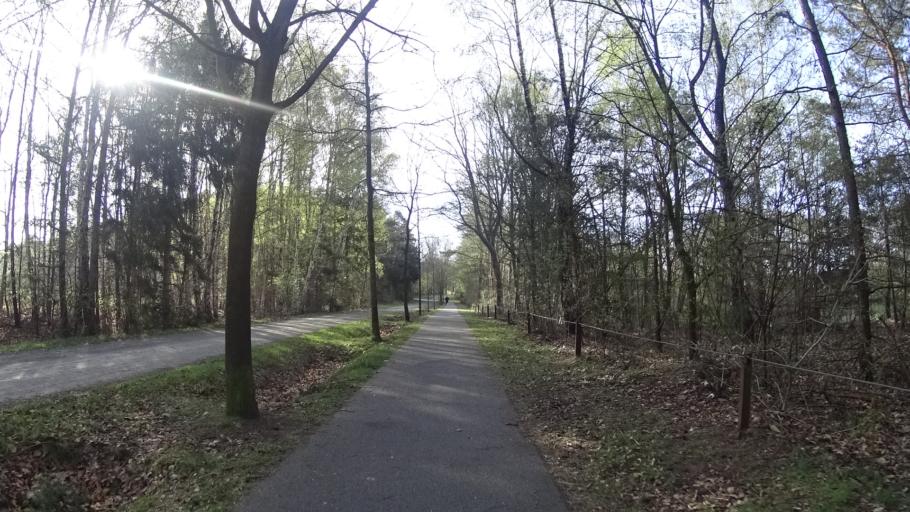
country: DE
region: Lower Saxony
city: Haren
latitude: 52.7924
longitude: 7.2712
